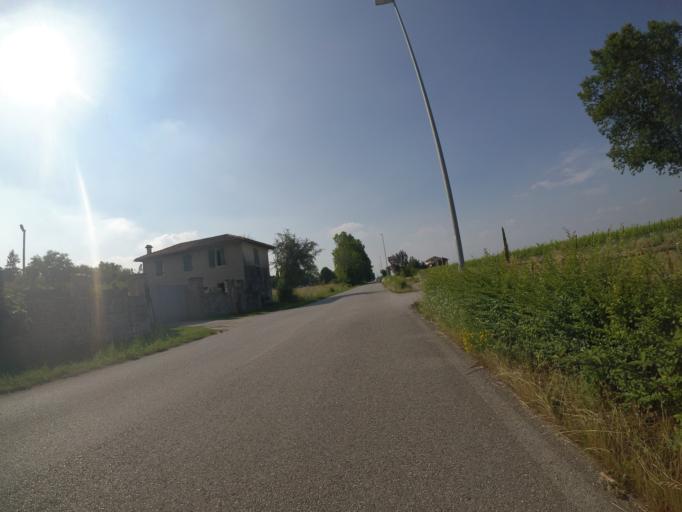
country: IT
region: Friuli Venezia Giulia
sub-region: Provincia di Udine
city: Camino al Tagliamento
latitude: 45.9305
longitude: 12.9593
